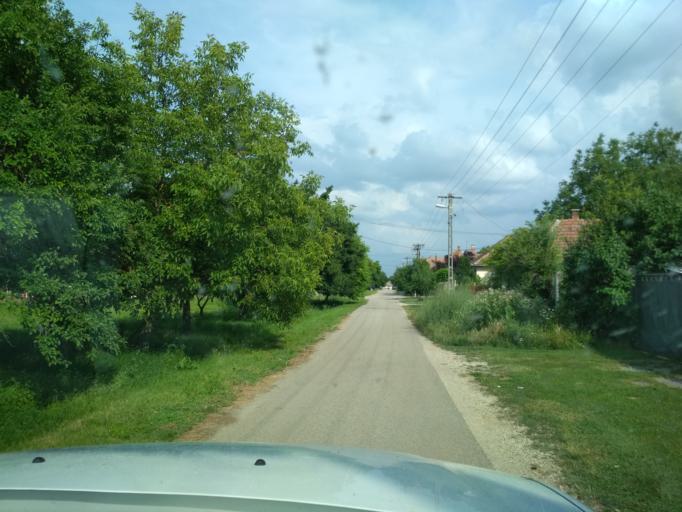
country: HU
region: Pest
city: Tapioszentmarton
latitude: 47.3329
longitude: 19.7507
